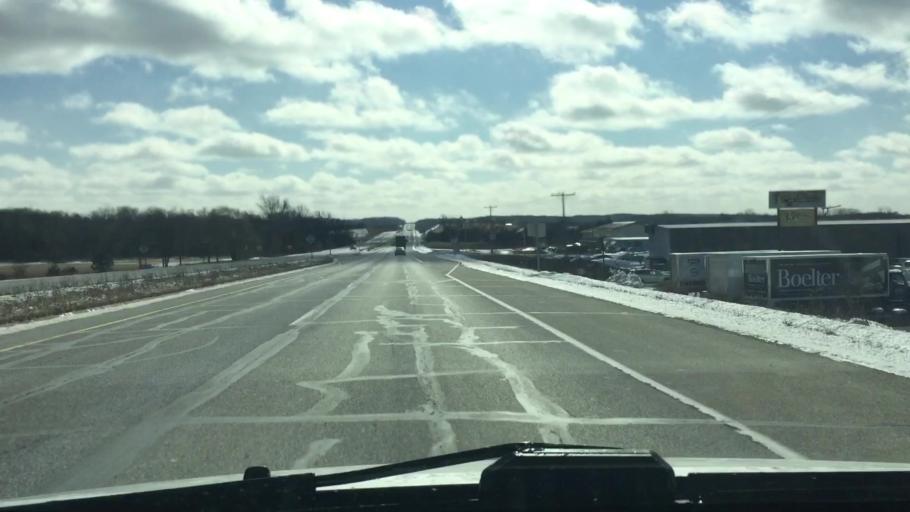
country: US
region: Wisconsin
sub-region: Waukesha County
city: Waukesha
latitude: 42.9723
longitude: -88.2278
